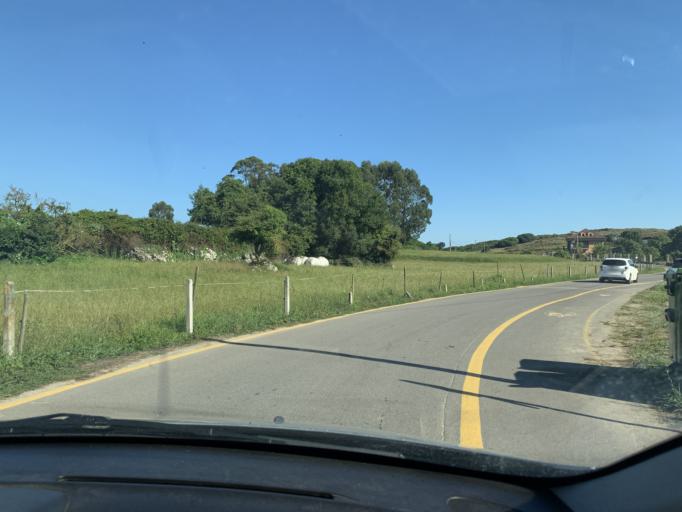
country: ES
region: Asturias
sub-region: Province of Asturias
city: Llanes
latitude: 43.4268
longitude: -4.7825
